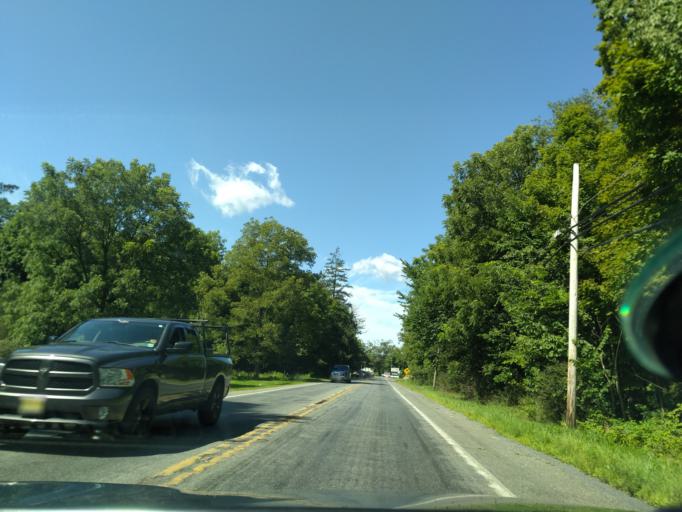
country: US
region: Pennsylvania
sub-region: Pike County
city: Saw Creek
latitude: 41.0817
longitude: -75.0201
